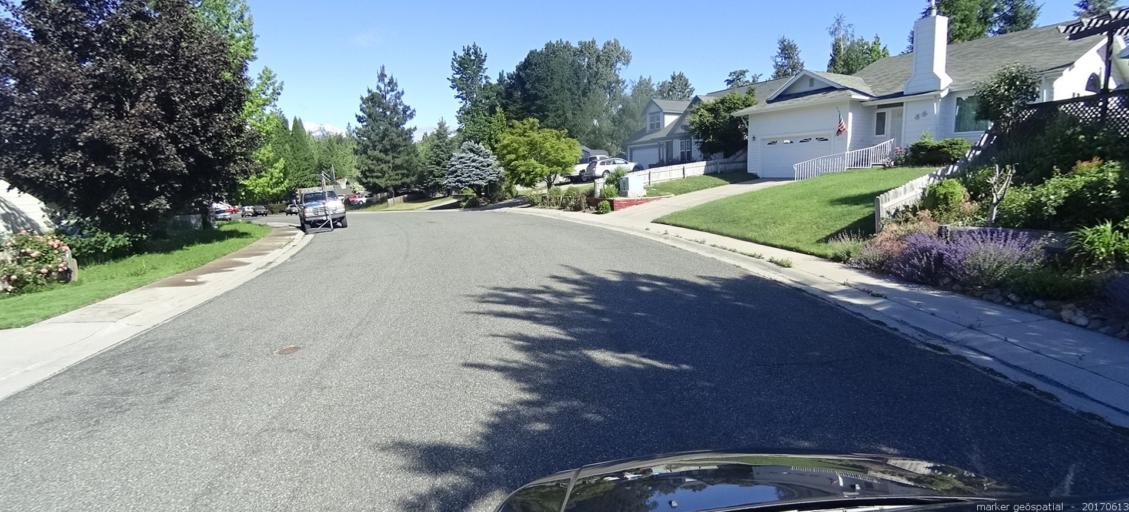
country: US
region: California
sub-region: Siskiyou County
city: Mount Shasta
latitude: 41.3037
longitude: -122.3040
